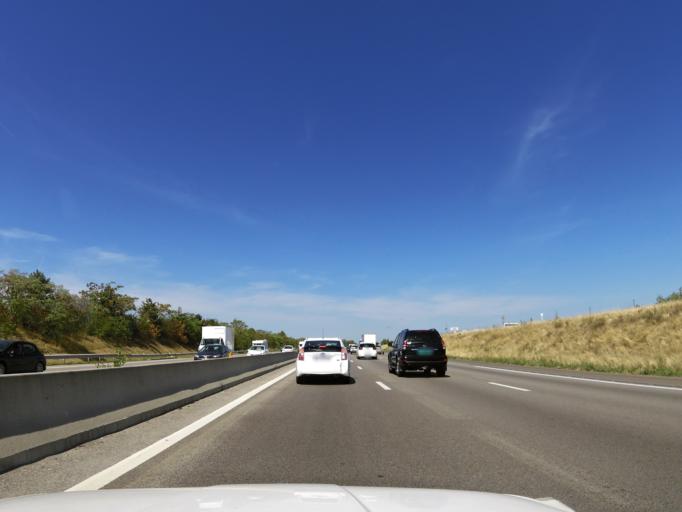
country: FR
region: Rhone-Alpes
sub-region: Departement de la Drome
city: Portes-les-Valence
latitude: 44.8730
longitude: 4.8648
